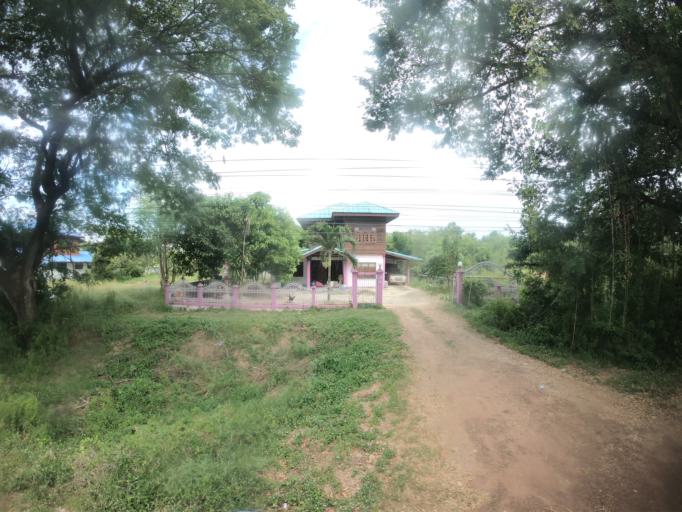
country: TH
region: Maha Sarakham
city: Chiang Yuen
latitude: 16.3444
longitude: 103.1283
